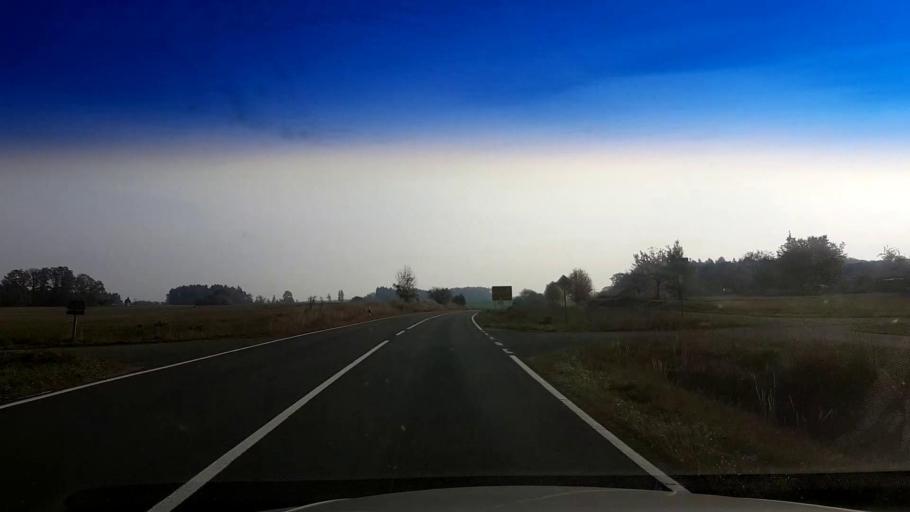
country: DE
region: Bavaria
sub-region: Upper Franconia
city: Stadelhofen
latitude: 50.0068
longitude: 11.1741
